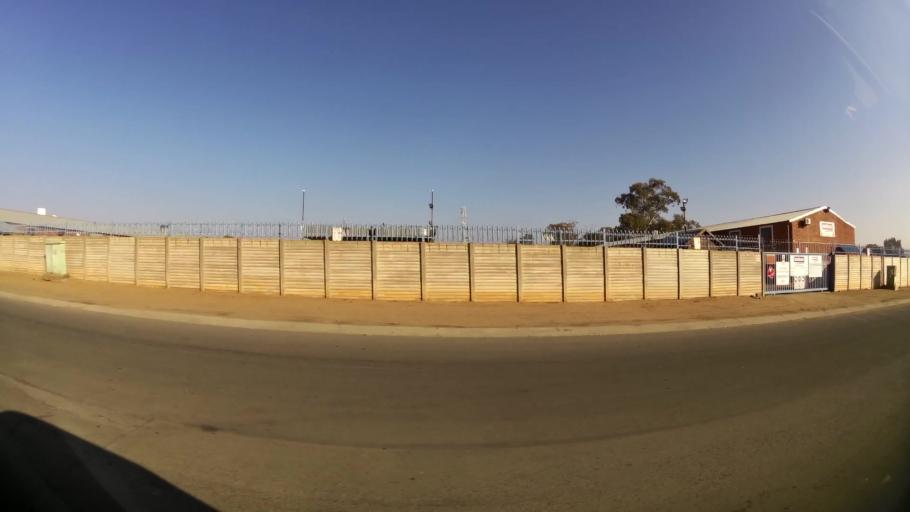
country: ZA
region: Orange Free State
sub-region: Mangaung Metropolitan Municipality
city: Bloemfontein
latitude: -29.1313
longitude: 26.2657
